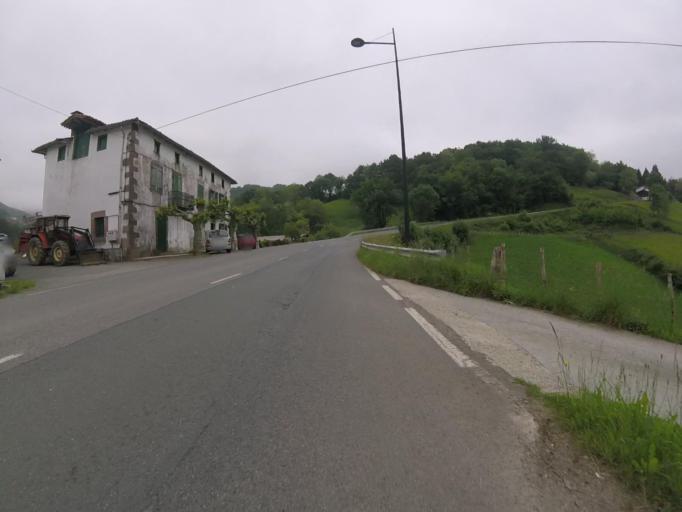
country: ES
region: Navarre
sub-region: Provincia de Navarra
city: Zugarramurdi
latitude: 43.2711
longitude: -1.4939
